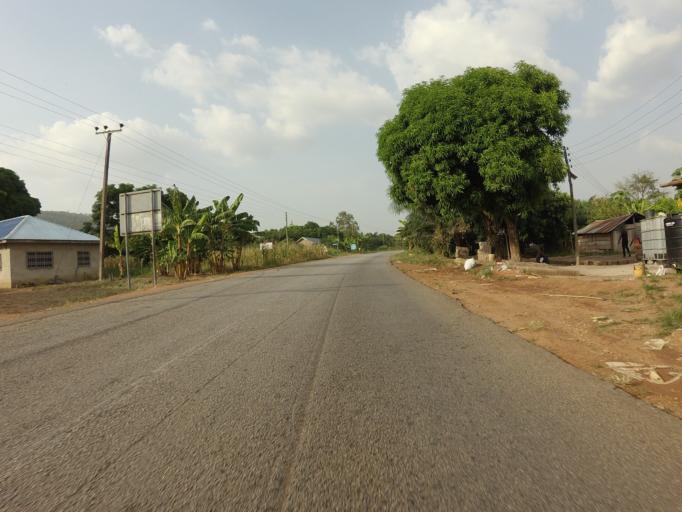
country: GH
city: Akropong
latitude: 6.2616
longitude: 0.1352
